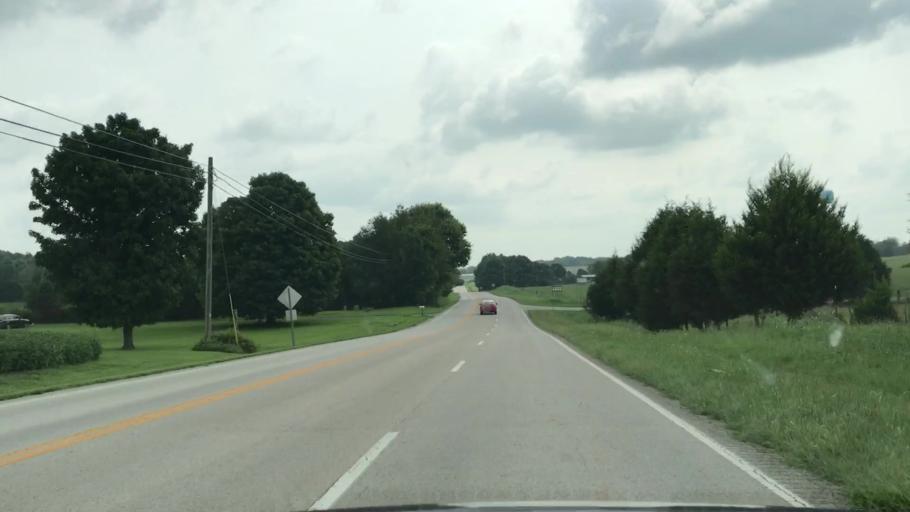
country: US
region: Kentucky
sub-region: Barren County
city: Cave City
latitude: 37.0915
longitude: -86.0838
